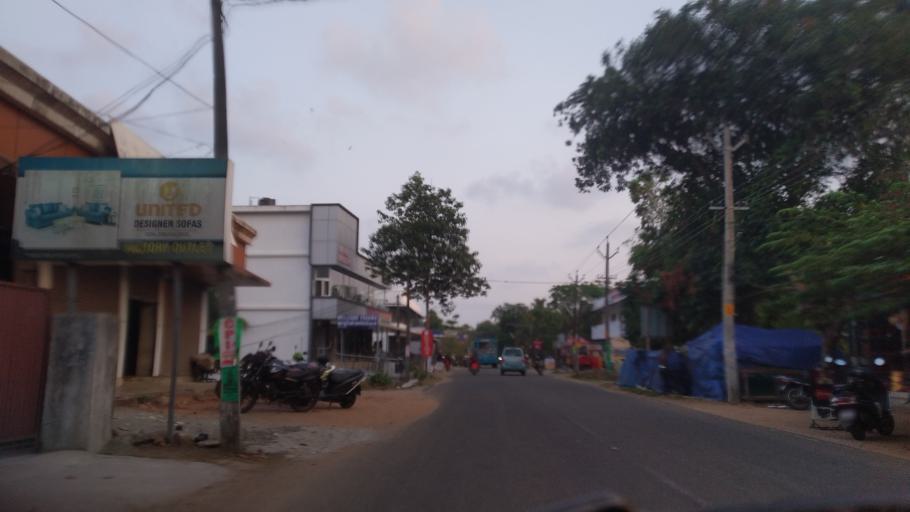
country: IN
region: Kerala
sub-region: Thrissur District
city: Kodungallur
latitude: 10.2171
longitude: 76.1602
